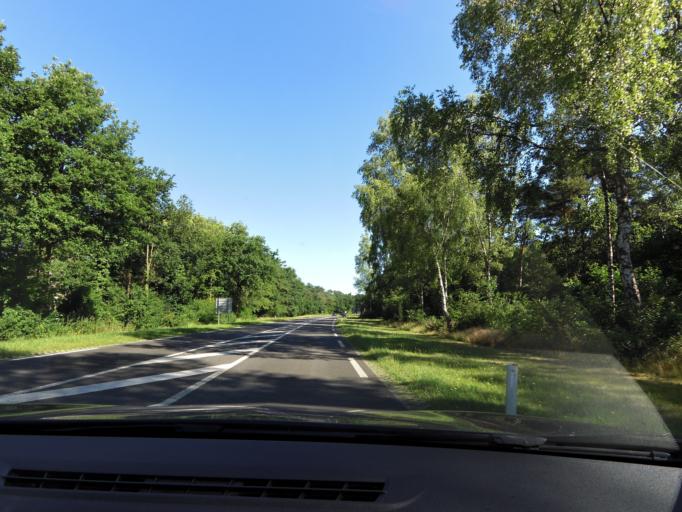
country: NL
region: Overijssel
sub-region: Gemeente Twenterand
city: Den Ham
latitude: 52.4923
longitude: 6.4239
